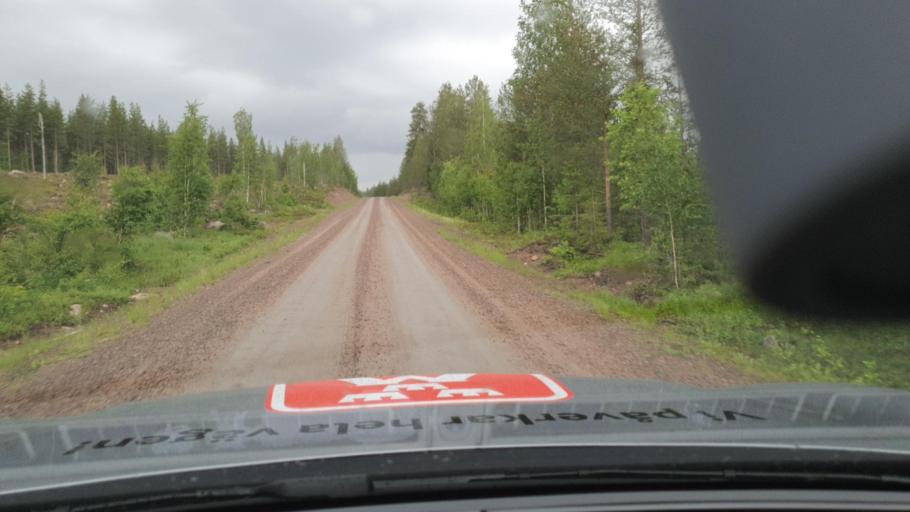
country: SE
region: Norrbotten
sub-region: Overkalix Kommun
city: OEverkalix
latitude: 66.6323
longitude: 22.7159
